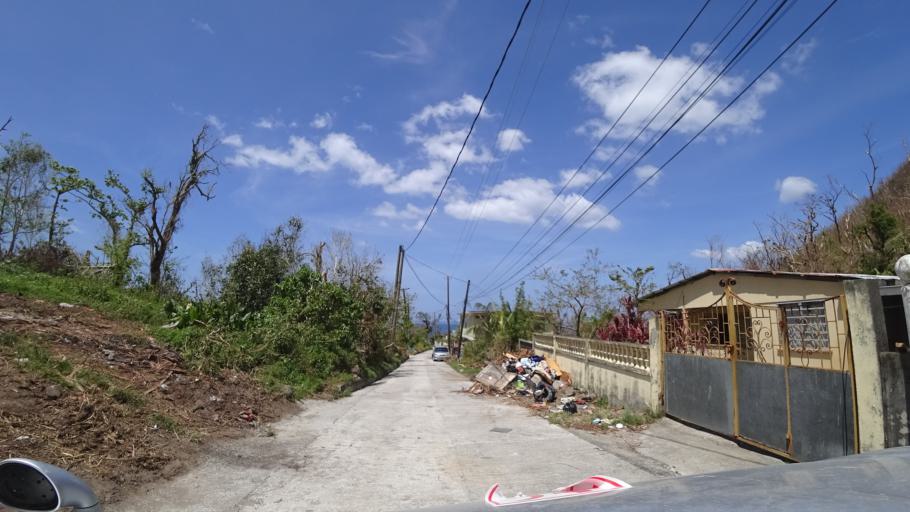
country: DM
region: Saint Luke
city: Pointe Michel
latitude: 15.2619
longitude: -61.3739
